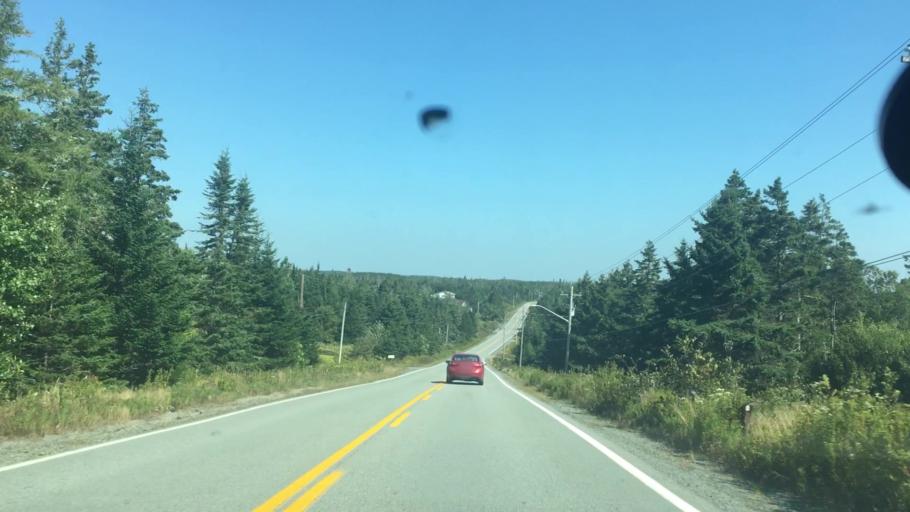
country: CA
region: Nova Scotia
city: Antigonish
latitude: 44.9401
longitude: -62.2675
